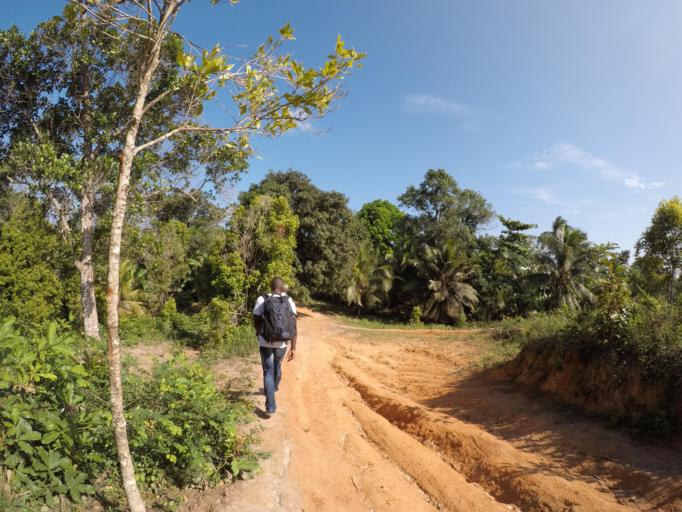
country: TZ
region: Pemba South
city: Mtambile
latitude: -5.3855
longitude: 39.7237
